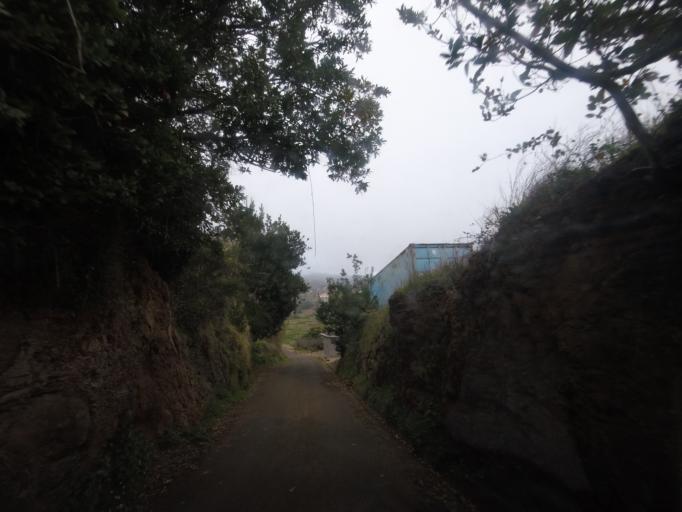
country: PT
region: Madeira
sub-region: Calheta
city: Faja da Ovelha
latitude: 32.7631
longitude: -17.2188
